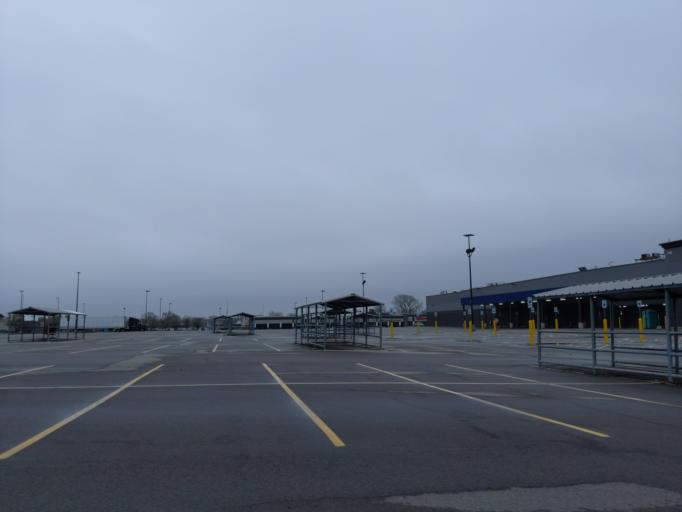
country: US
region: Michigan
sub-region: Ingham County
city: Holt
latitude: 42.6621
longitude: -84.5478
